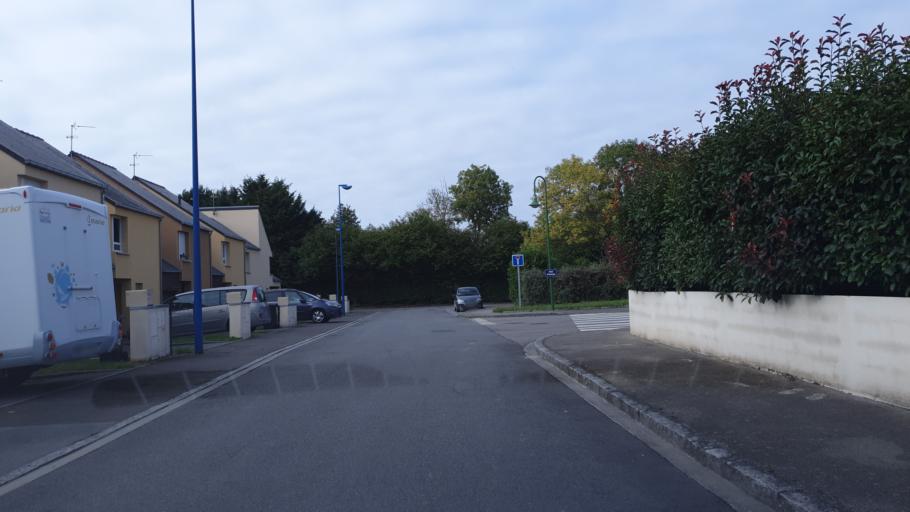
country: FR
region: Brittany
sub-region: Departement d'Ille-et-Vilaine
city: Janze
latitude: 47.9503
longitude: -1.4937
